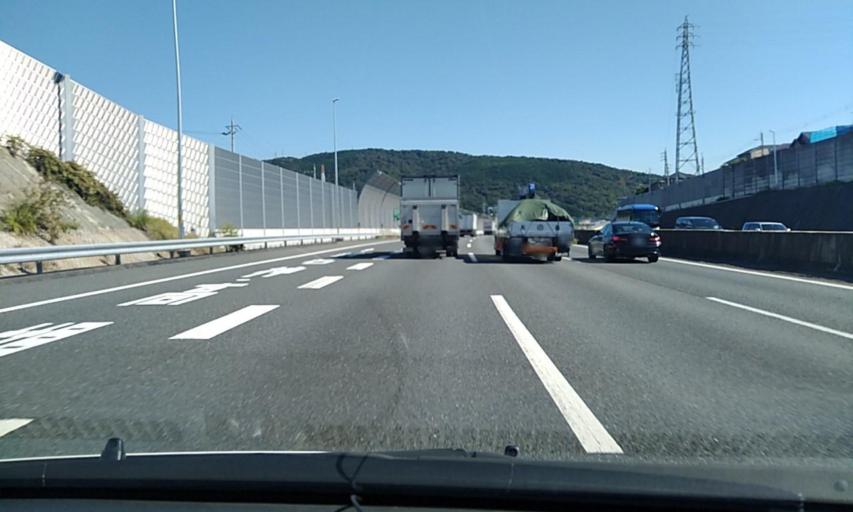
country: JP
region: Osaka
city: Takatsuki
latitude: 34.8676
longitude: 135.6170
